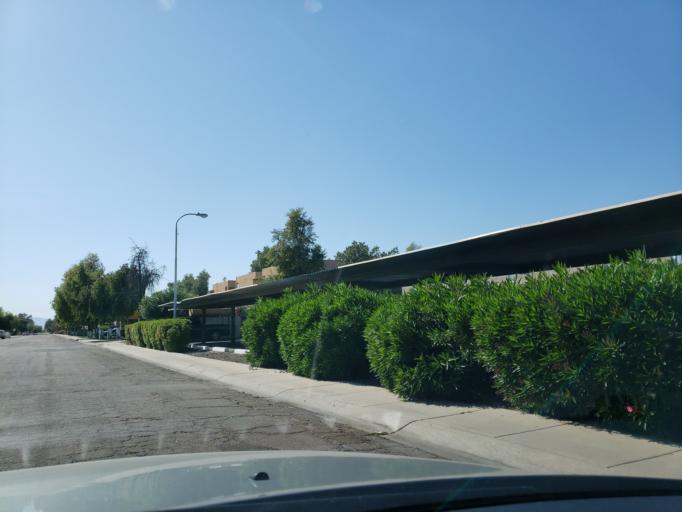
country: US
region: Arizona
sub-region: Maricopa County
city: Glendale
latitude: 33.5567
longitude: -112.1880
